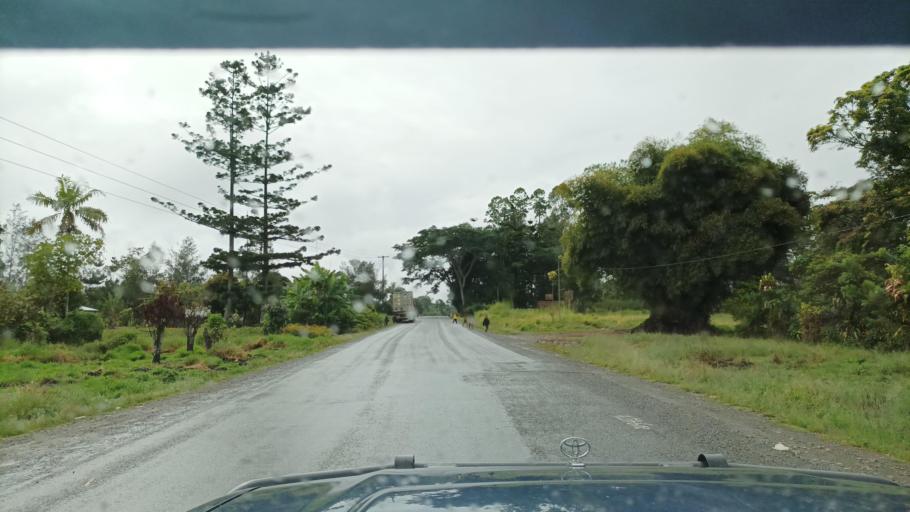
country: PG
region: Jiwaka
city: Minj
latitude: -5.8735
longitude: 144.6612
